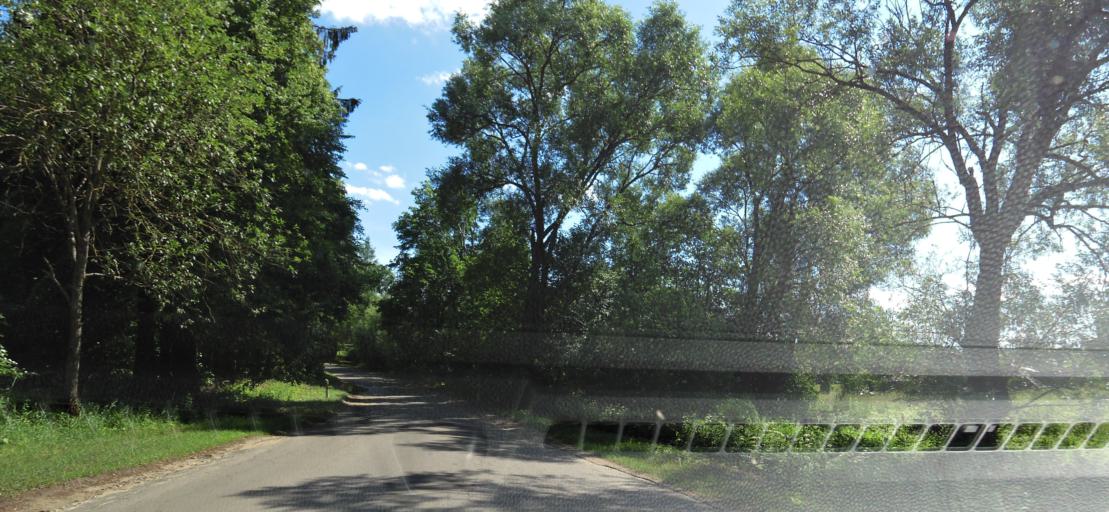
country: LT
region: Vilnius County
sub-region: Vilnius
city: Fabijoniskes
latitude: 54.8141
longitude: 25.3218
